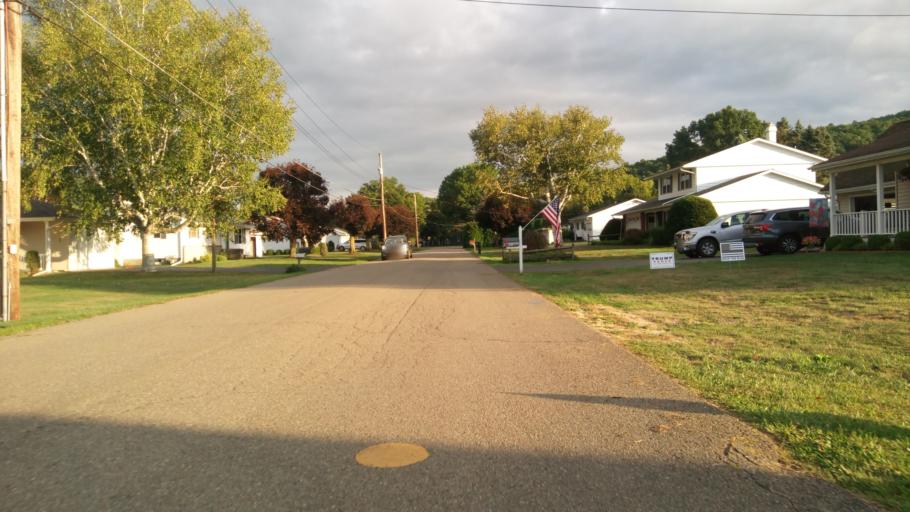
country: US
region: New York
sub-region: Chemung County
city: Southport
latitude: 42.0542
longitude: -76.8318
